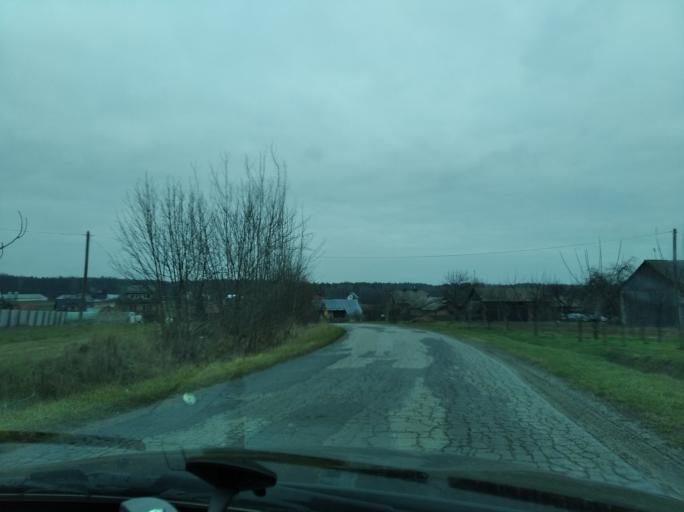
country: PL
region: Subcarpathian Voivodeship
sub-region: Powiat lancucki
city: Brzoza Stadnicka
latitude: 50.1895
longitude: 22.2571
